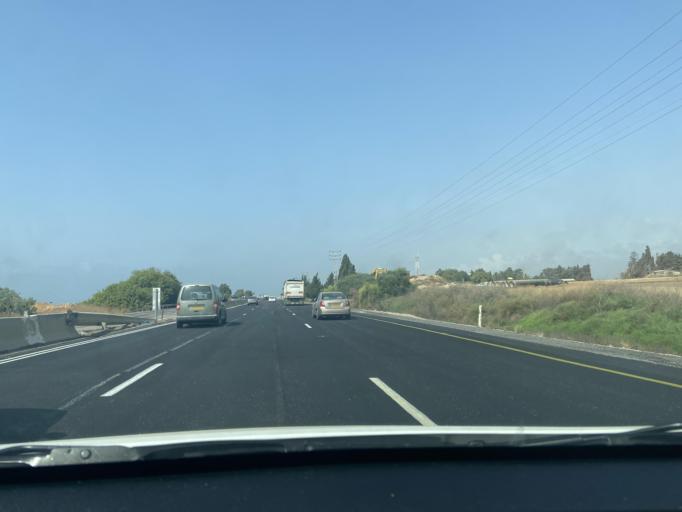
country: IL
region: Northern District
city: El Mazra`a
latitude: 32.9652
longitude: 35.0936
